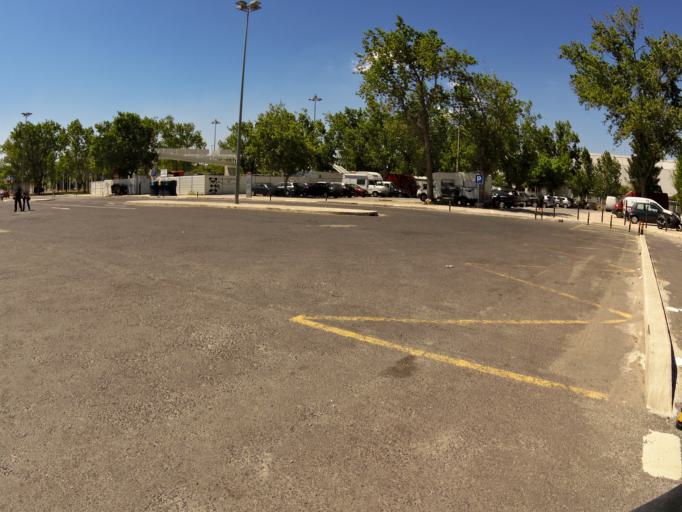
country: PT
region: Setubal
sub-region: Almada
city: Caparica
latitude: 38.6951
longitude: -9.1978
